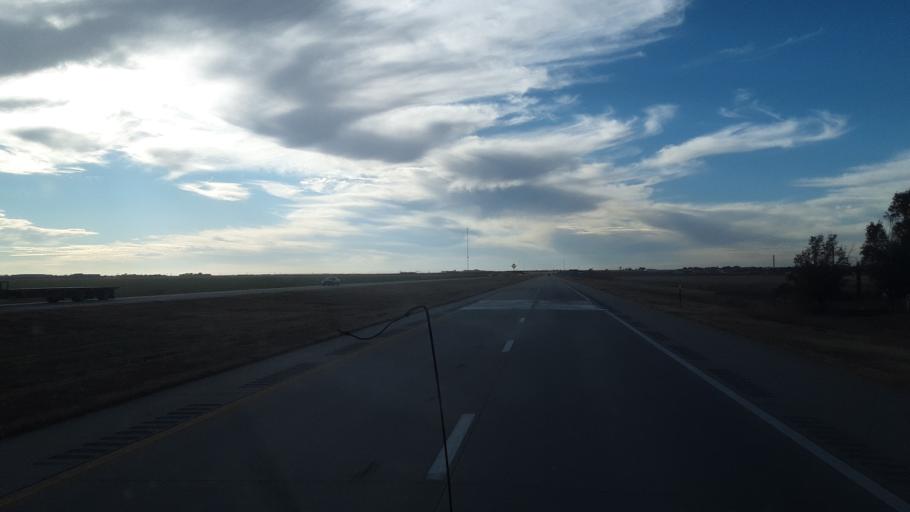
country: US
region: Kansas
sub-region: Finney County
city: Holcomb
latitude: 38.0034
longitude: -100.9746
